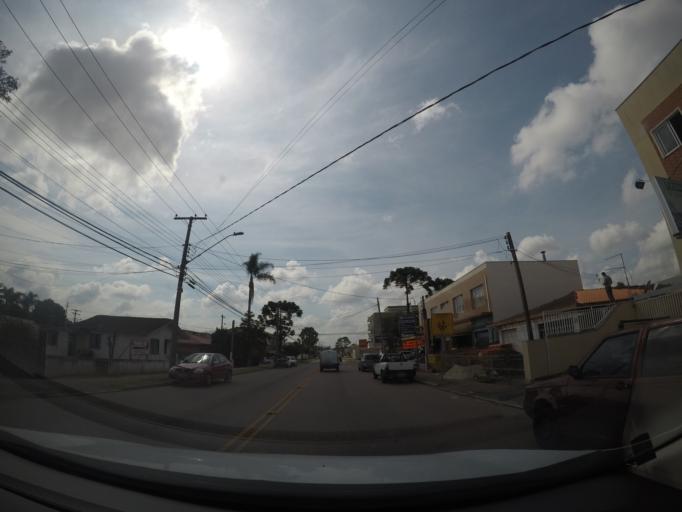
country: BR
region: Parana
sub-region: Curitiba
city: Curitiba
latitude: -25.4795
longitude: -49.2676
